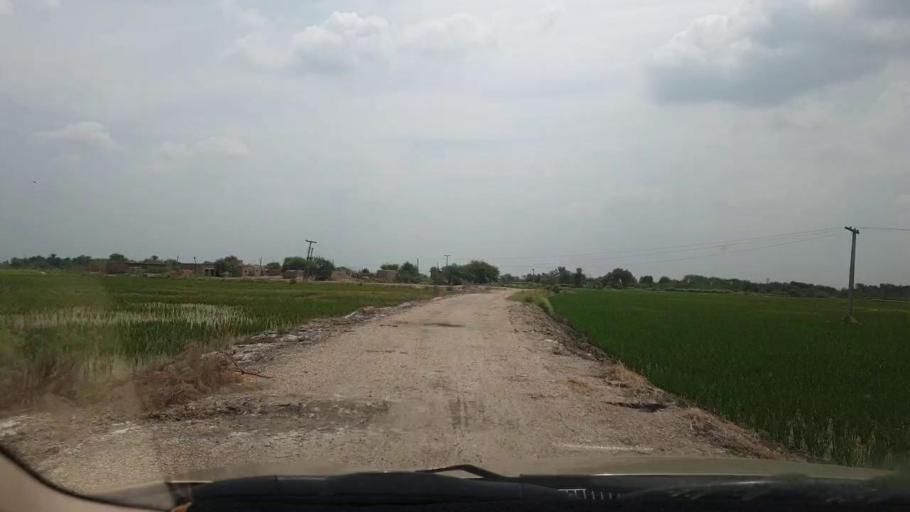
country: PK
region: Sindh
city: Larkana
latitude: 27.5384
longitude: 68.1425
